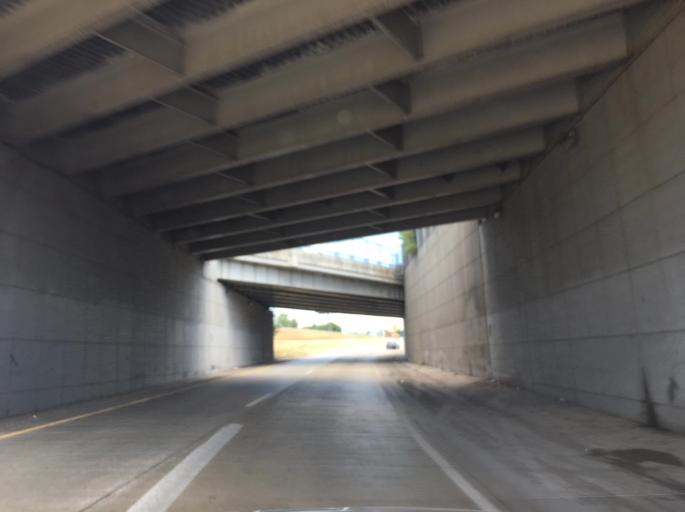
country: US
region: Michigan
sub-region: Wayne County
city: Highland Park
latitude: 42.4084
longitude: -83.0769
